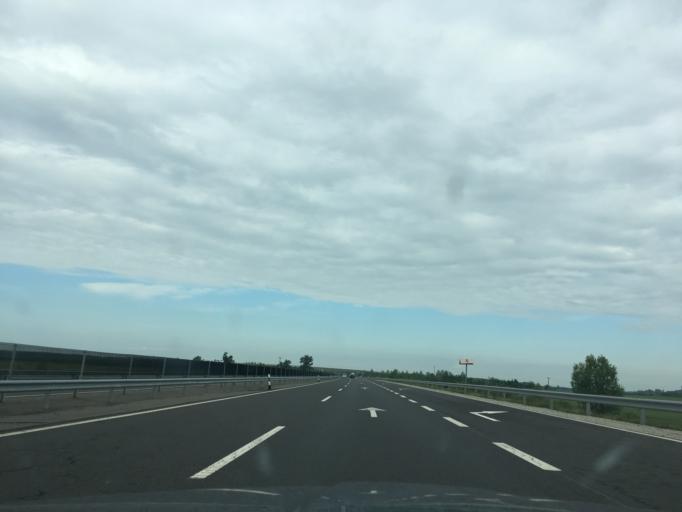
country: HU
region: Hajdu-Bihar
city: Balmazujvaros
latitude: 47.7261
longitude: 21.4005
